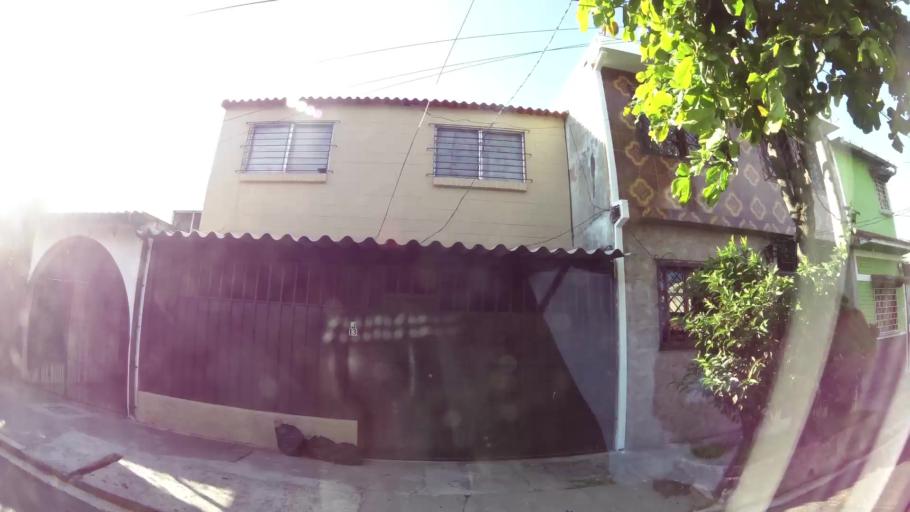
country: SV
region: La Libertad
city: Santa Tecla
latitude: 13.6809
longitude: -89.2836
